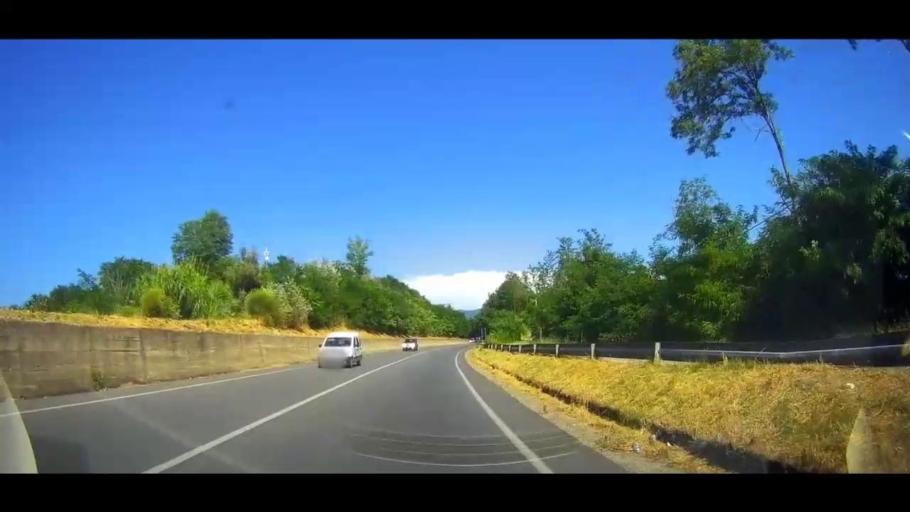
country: IT
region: Calabria
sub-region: Provincia di Cosenza
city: Zumpano
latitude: 39.2985
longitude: 16.2834
